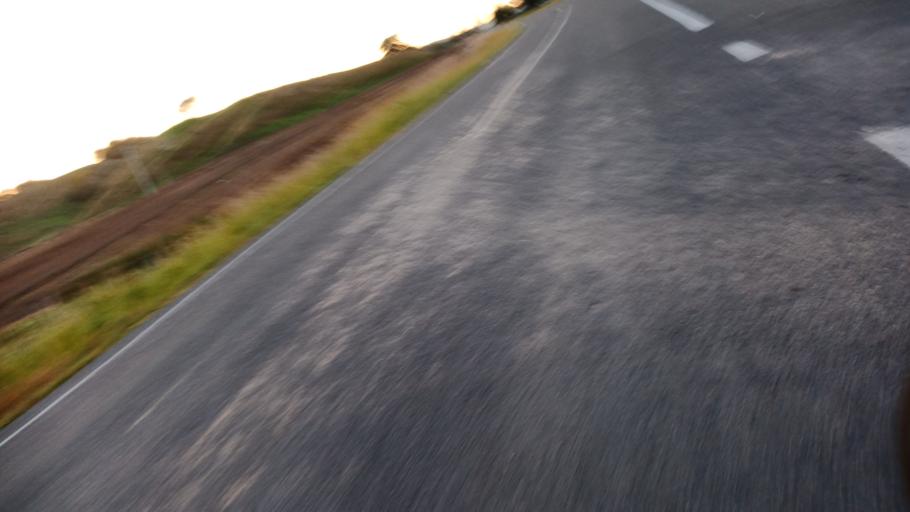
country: NZ
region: Gisborne
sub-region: Gisborne District
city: Gisborne
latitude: -38.6317
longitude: 177.9921
